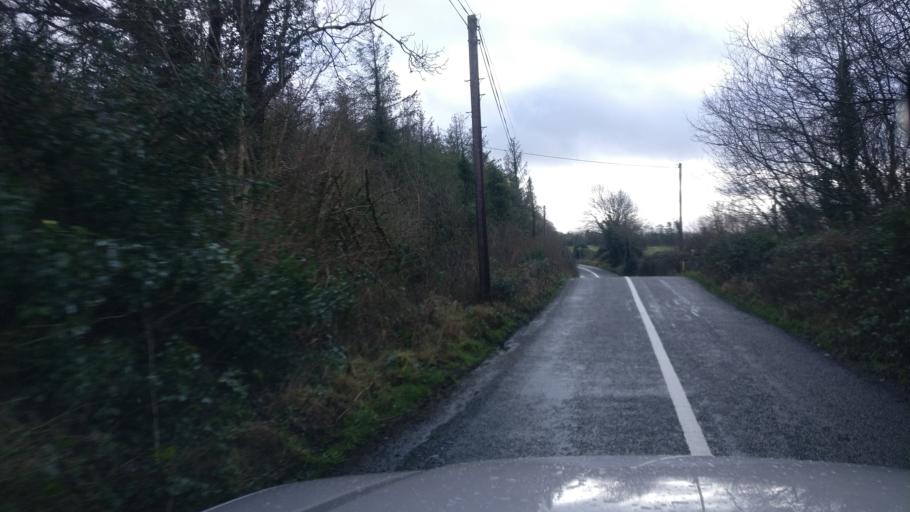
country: IE
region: Connaught
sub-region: County Galway
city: Loughrea
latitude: 53.2510
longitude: -8.6225
